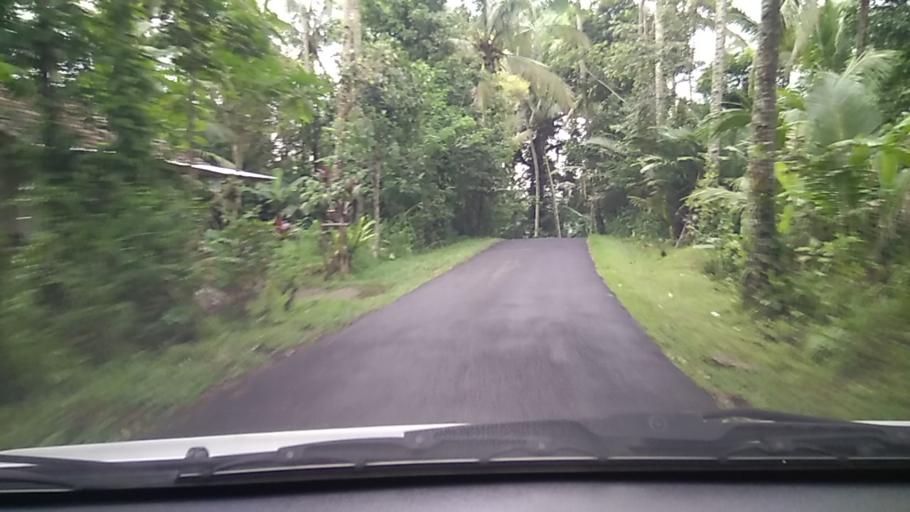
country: ID
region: Bali
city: Banjar Dujung Kaja
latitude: -8.4116
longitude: 115.2866
